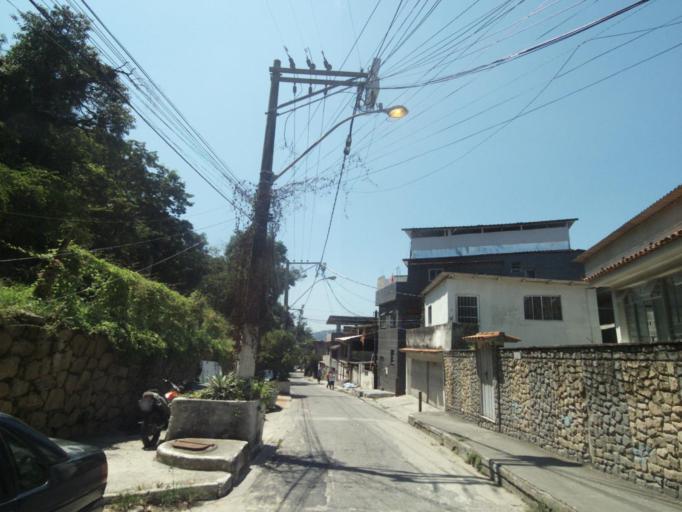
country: BR
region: Rio de Janeiro
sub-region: Niteroi
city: Niteroi
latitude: -22.9273
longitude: -43.1214
